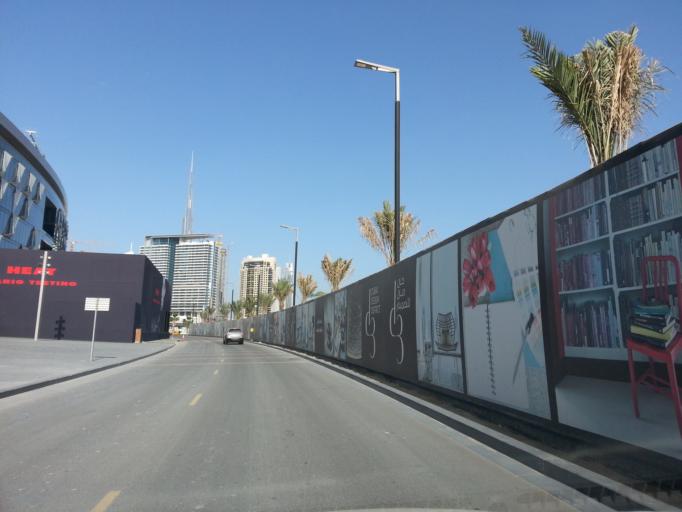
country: AE
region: Dubai
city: Dubai
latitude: 25.1901
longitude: 55.2981
